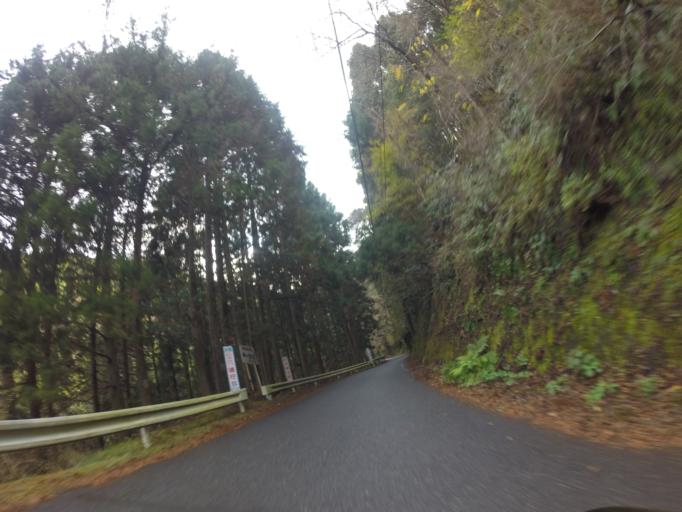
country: JP
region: Shizuoka
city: Heda
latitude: 34.8227
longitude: 138.8374
